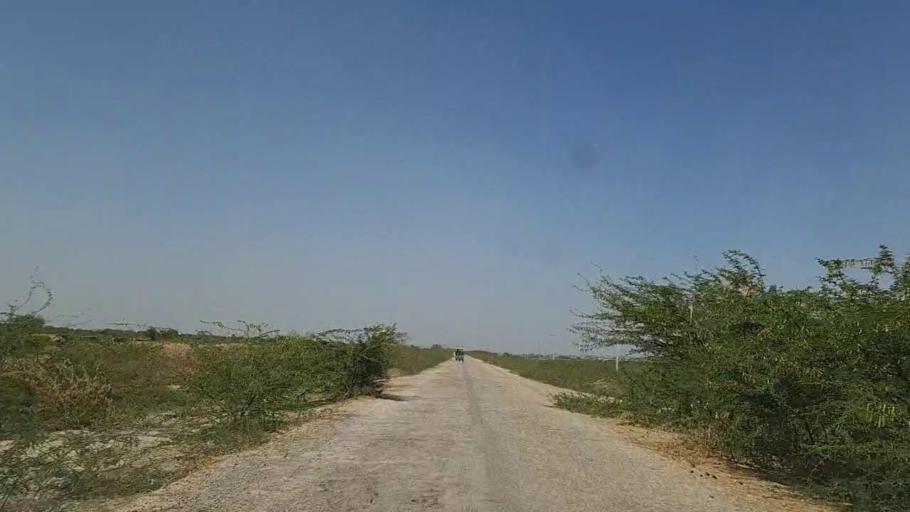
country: PK
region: Sindh
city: Naukot
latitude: 24.6412
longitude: 69.2879
